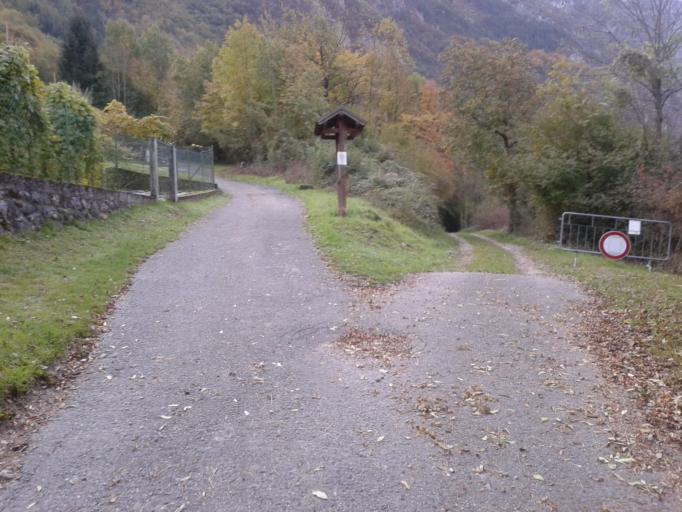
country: IT
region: Trentino-Alto Adige
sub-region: Provincia di Trento
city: Condino
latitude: 45.8838
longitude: 10.6010
